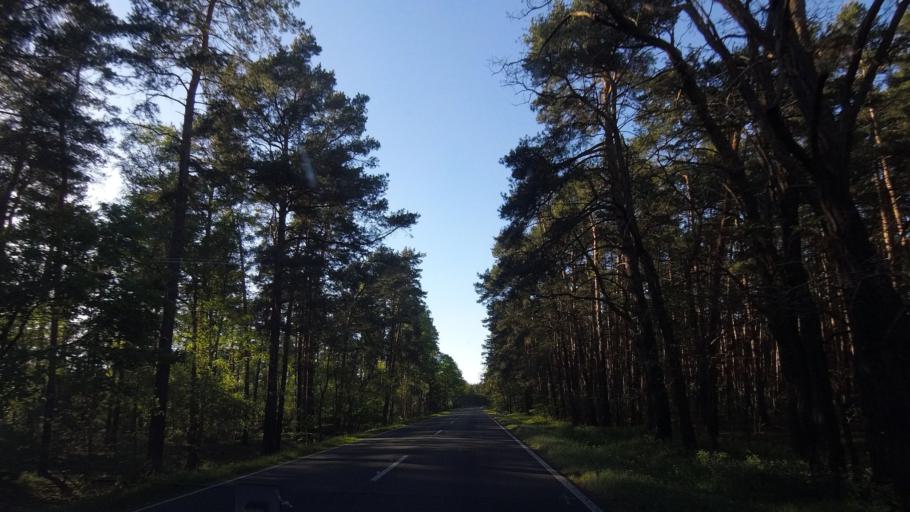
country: DE
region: Brandenburg
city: Golssen
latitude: 52.0058
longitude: 13.5544
